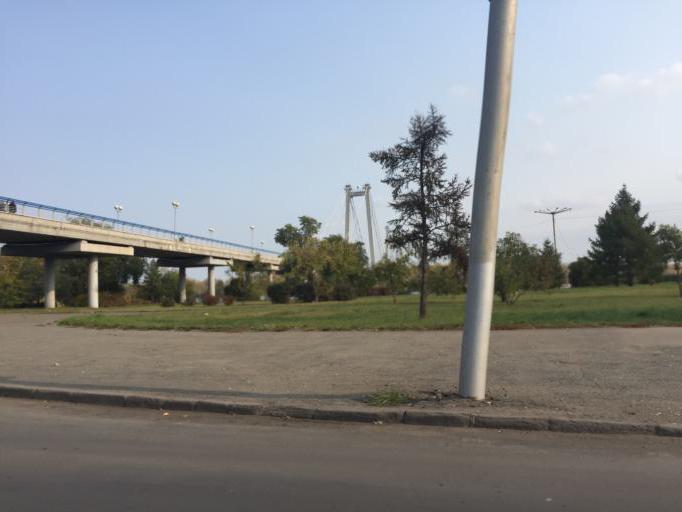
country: RU
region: Krasnoyarskiy
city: Krasnoyarsk
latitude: 56.0133
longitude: 92.8967
